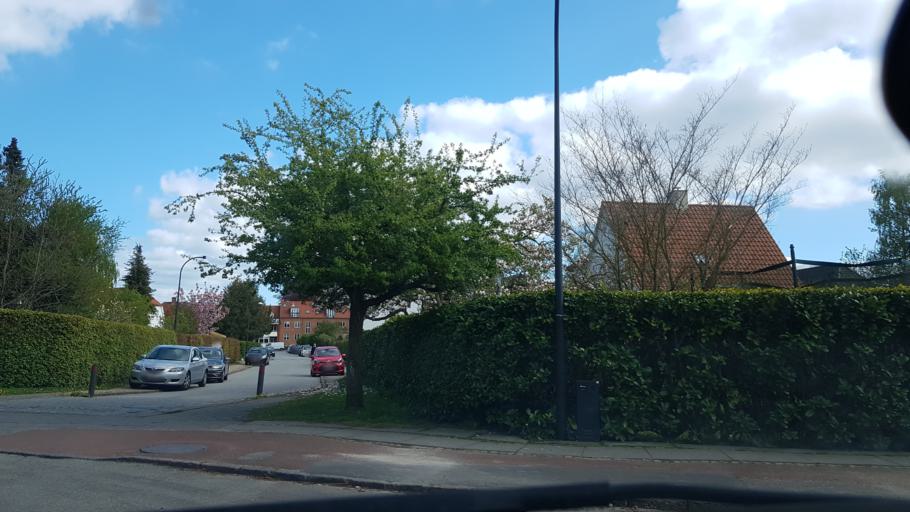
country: DK
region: Capital Region
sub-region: Rudersdal Kommune
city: Holte
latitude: 55.8152
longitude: 12.4676
